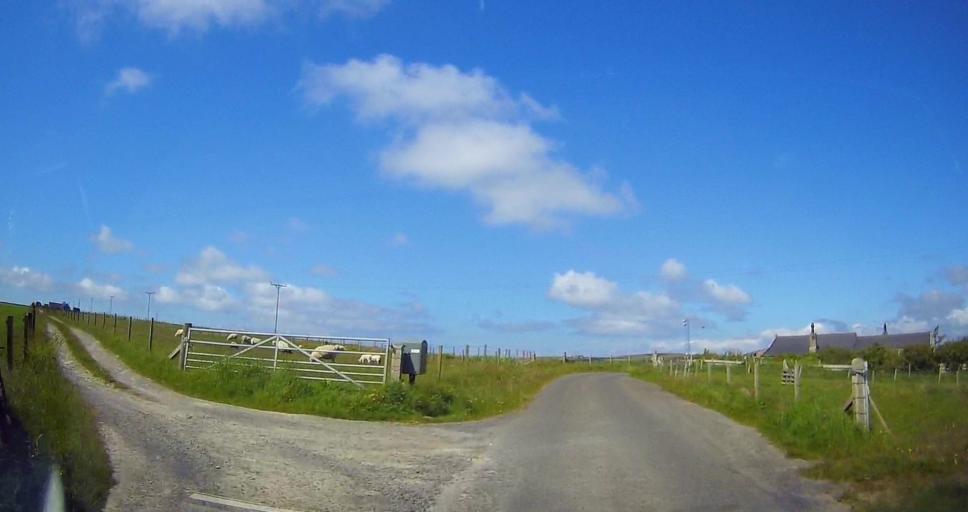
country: GB
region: Scotland
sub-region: Orkney Islands
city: Kirkwall
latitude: 58.8354
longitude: -2.9019
